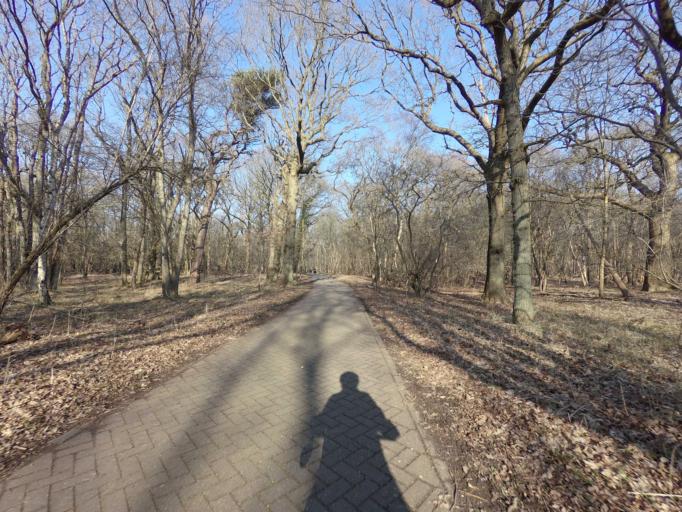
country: NL
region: North Holland
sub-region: Gemeente Velsen
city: Velsen-Zuid
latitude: 52.4480
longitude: 4.6121
